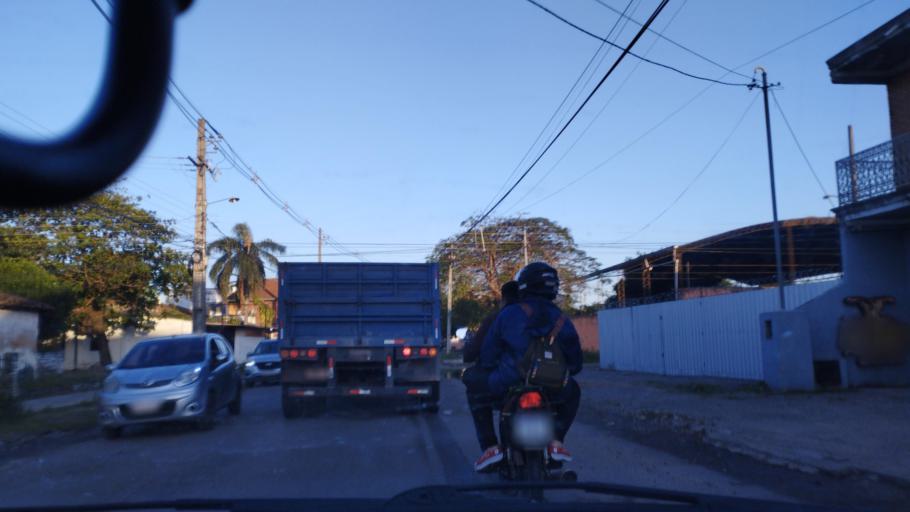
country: PY
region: Central
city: Fernando de la Mora
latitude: -25.2990
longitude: -57.5505
